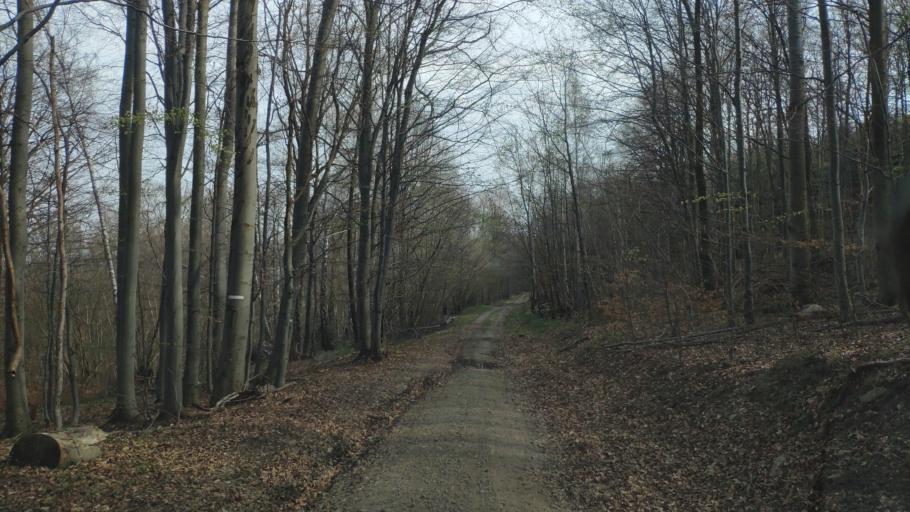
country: SK
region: Kosicky
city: Moldava nad Bodvou
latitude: 48.7381
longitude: 21.0554
